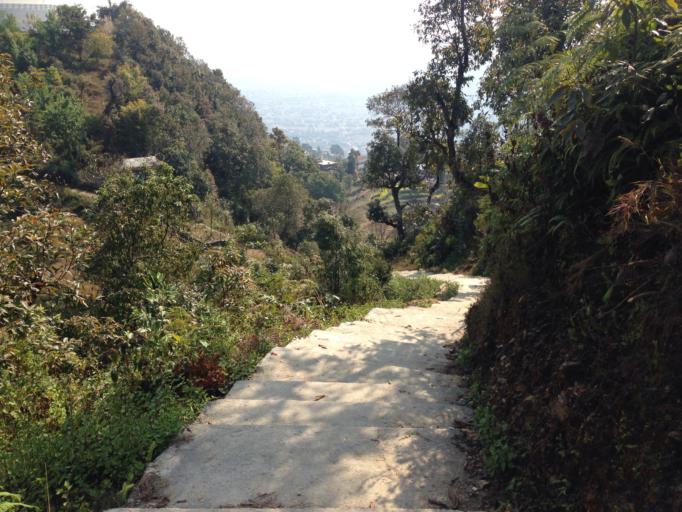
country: NP
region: Western Region
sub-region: Gandaki Zone
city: Pokhara
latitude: 28.2015
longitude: 83.9431
